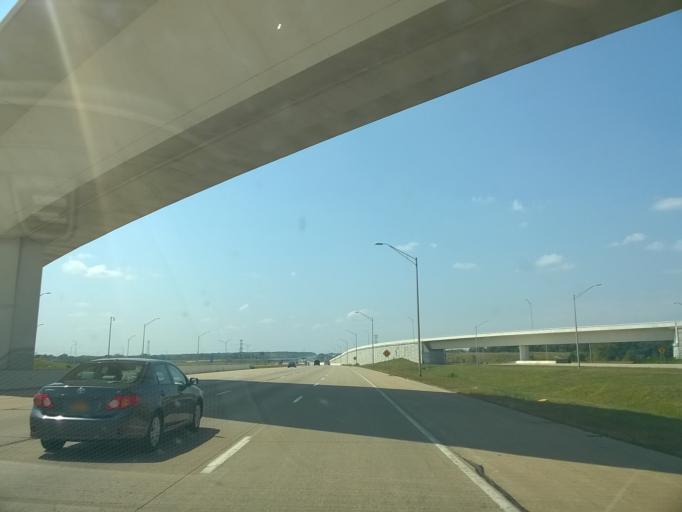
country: US
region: Indiana
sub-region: Hendricks County
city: Plainfield
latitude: 39.6883
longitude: -86.3232
